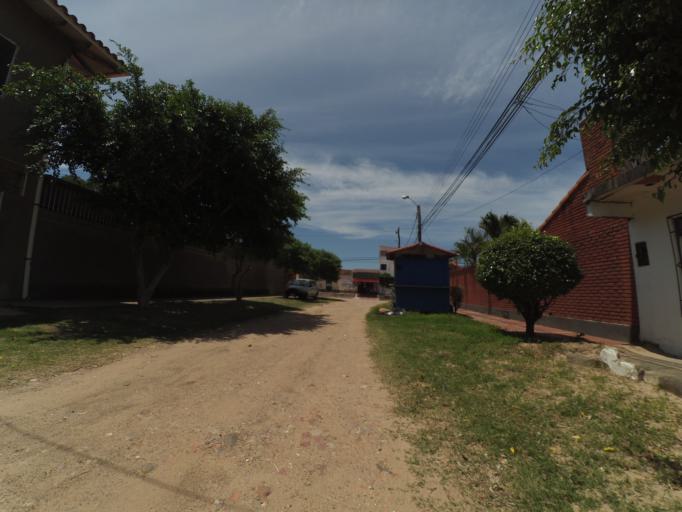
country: BO
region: Santa Cruz
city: Santa Cruz de la Sierra
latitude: -17.8111
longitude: -63.2232
